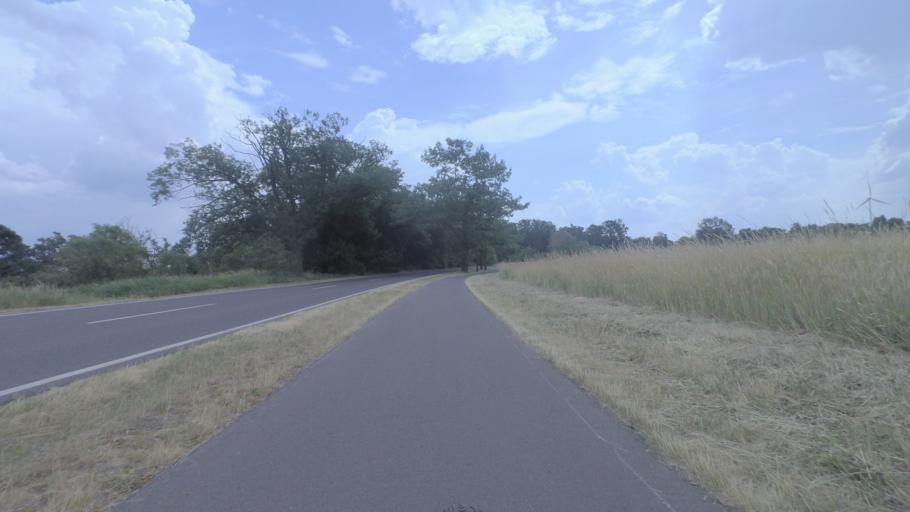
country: DE
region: Brandenburg
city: Grossbeeren
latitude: 52.3450
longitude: 13.2773
